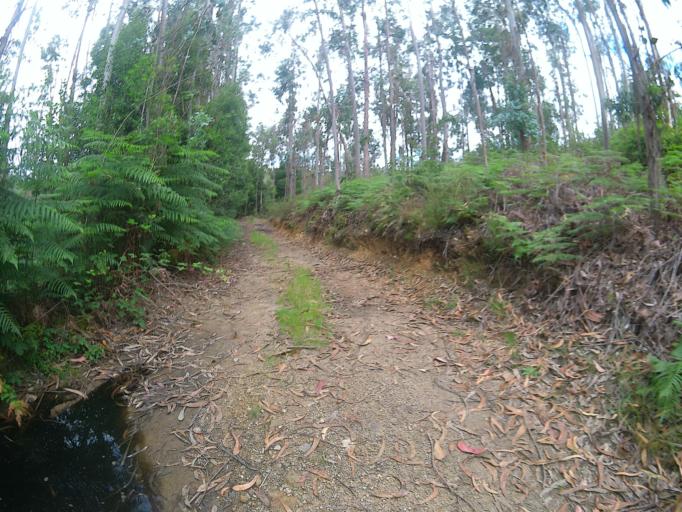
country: PT
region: Aveiro
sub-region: Albergaria-A-Velha
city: Branca
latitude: 40.7695
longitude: -8.4353
